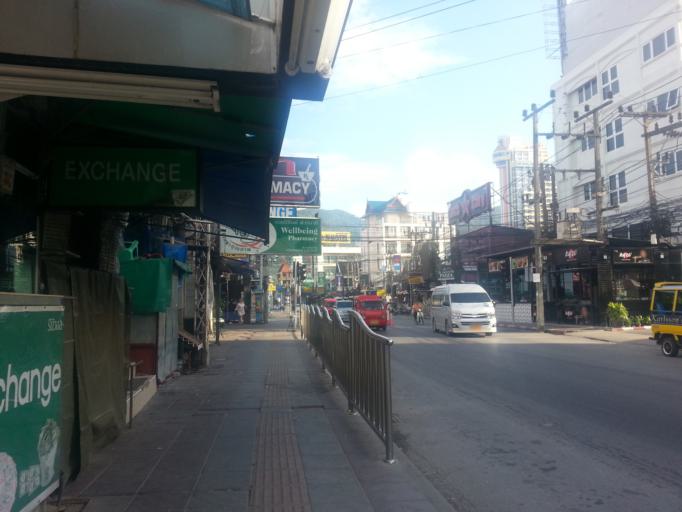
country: TH
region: Phuket
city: Patong
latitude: 7.8927
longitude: 98.2982
